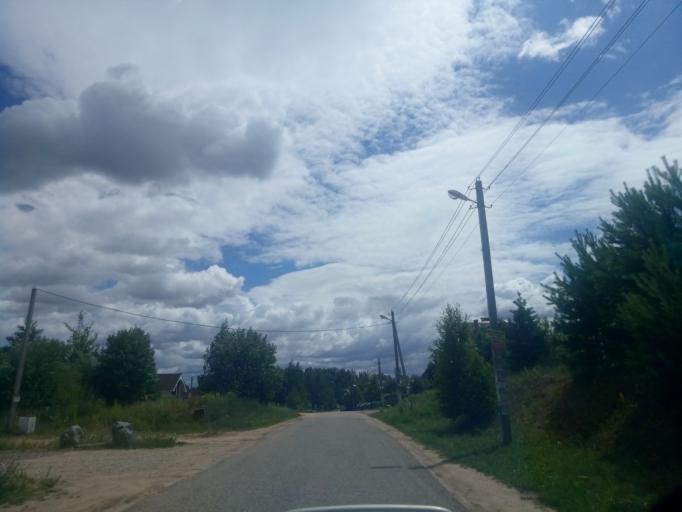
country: BY
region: Minsk
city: Zhdanovichy
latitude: 53.9384
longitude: 27.4096
